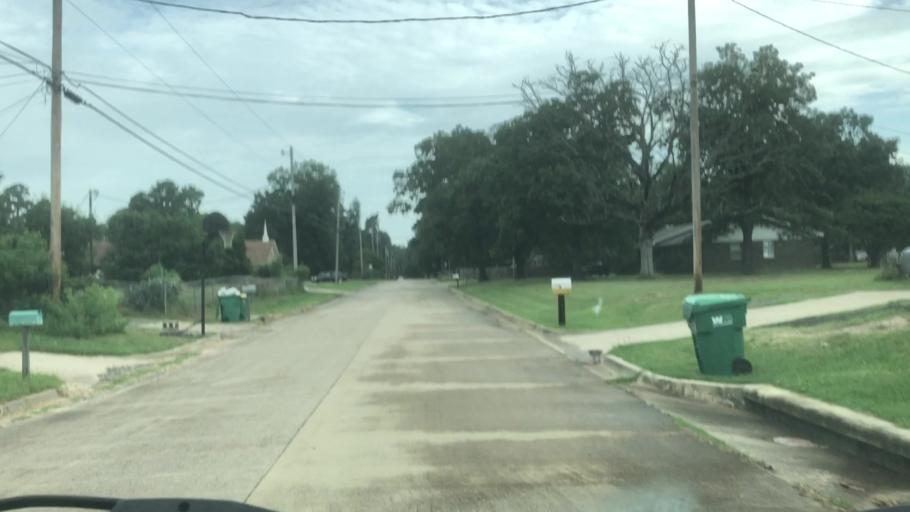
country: US
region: Texas
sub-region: Bowie County
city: Wake Village
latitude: 33.3901
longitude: -94.0856
